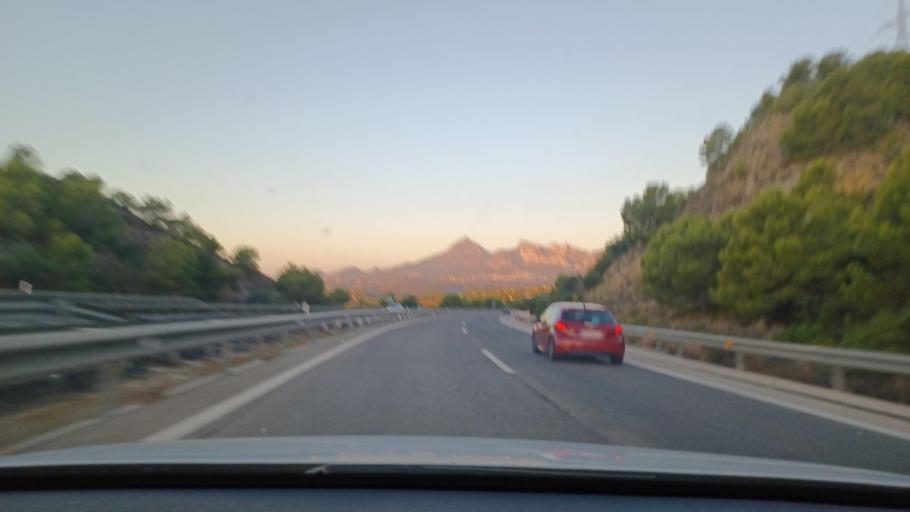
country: ES
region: Valencia
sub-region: Provincia de Alicante
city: Calp
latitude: 38.6334
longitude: -0.0028
